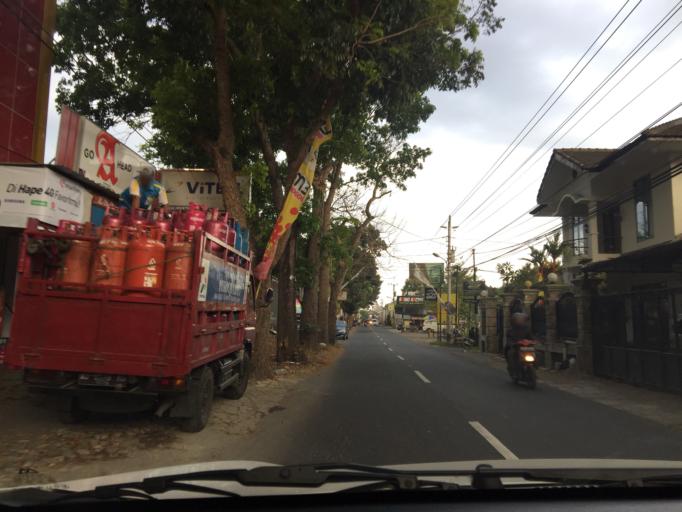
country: ID
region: Daerah Istimewa Yogyakarta
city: Melati
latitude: -7.7337
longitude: 110.3883
